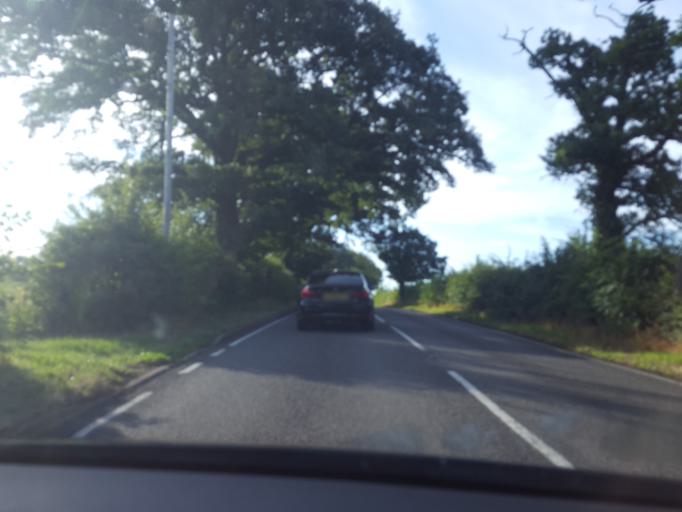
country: GB
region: England
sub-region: Leicestershire
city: Shepshed
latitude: 52.7426
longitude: -1.2716
